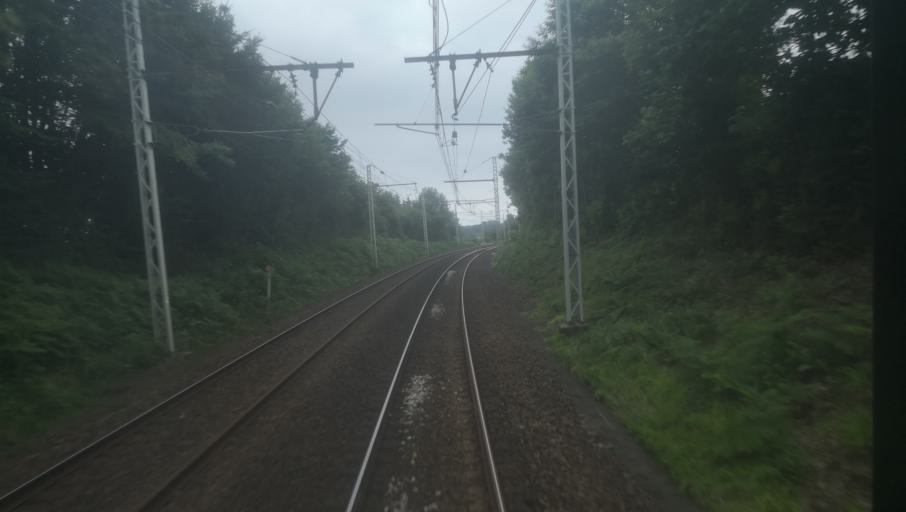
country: FR
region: Centre
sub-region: Departement de l'Indre
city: Chantome
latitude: 46.4025
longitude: 1.5445
